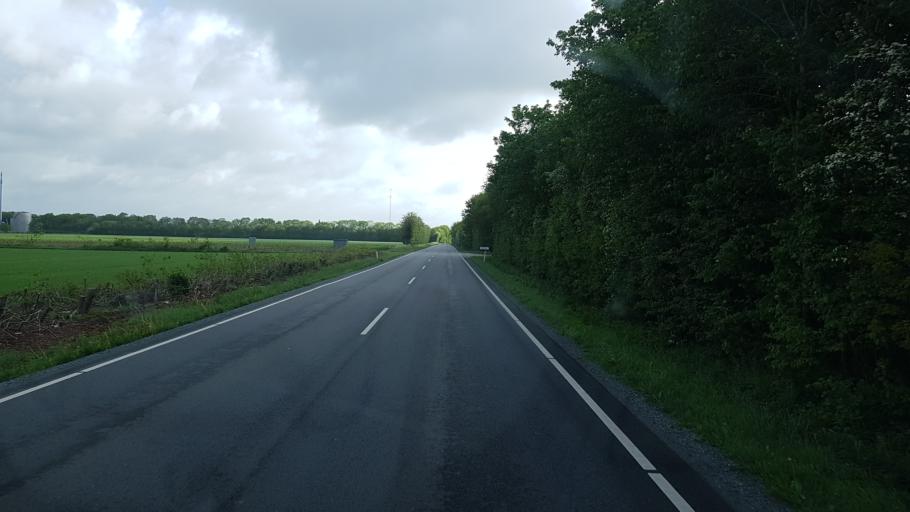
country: DK
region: South Denmark
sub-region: Vejen Kommune
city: Vejen
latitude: 55.4626
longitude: 9.1703
